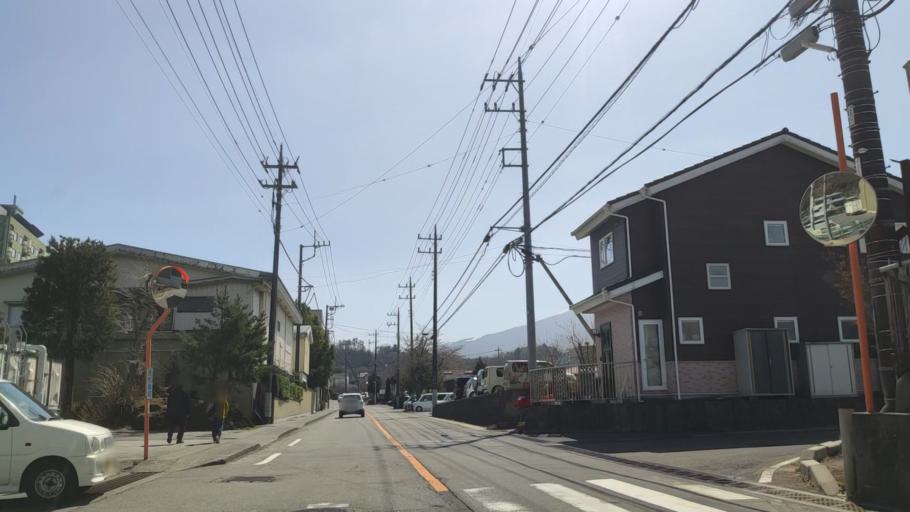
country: JP
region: Yamanashi
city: Fujikawaguchiko
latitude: 35.4682
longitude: 138.8128
